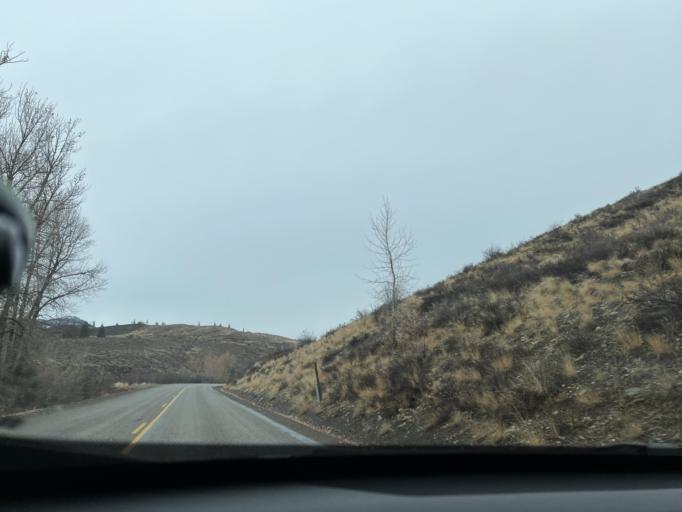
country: US
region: Washington
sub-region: Chelan County
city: Granite Falls
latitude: 48.4632
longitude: -120.2454
